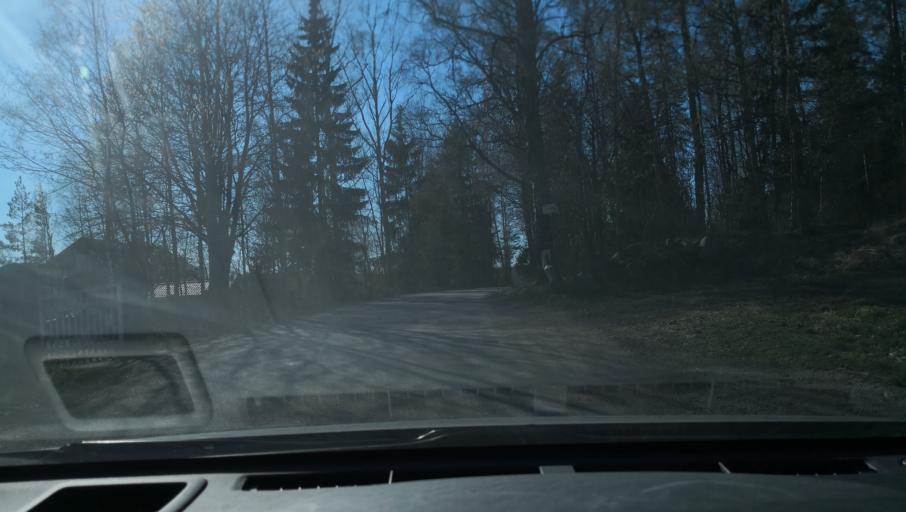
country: SE
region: Vaestmanland
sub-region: Sala Kommun
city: Sala
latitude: 60.0767
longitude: 16.4808
